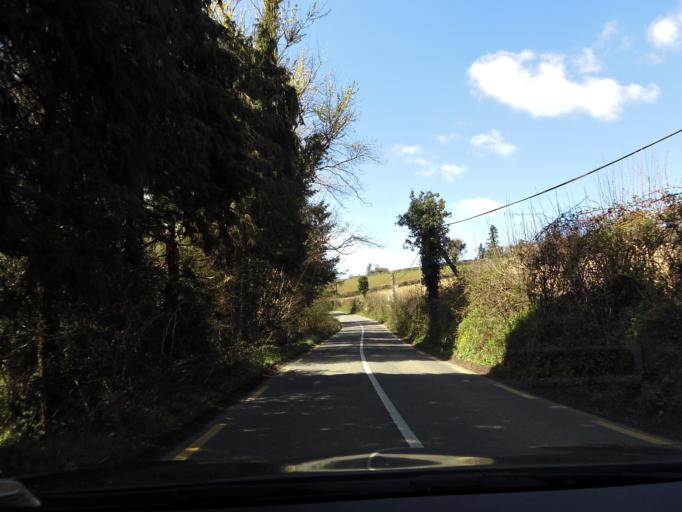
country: IE
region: Leinster
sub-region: Wicklow
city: Aughrim
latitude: 52.8493
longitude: -6.2838
